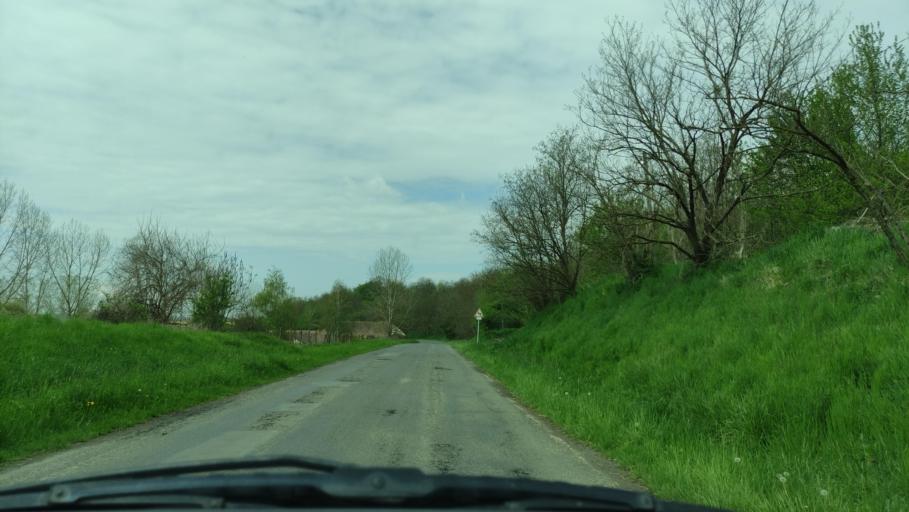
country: HU
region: Baranya
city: Sasd
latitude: 46.3061
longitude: 18.1575
